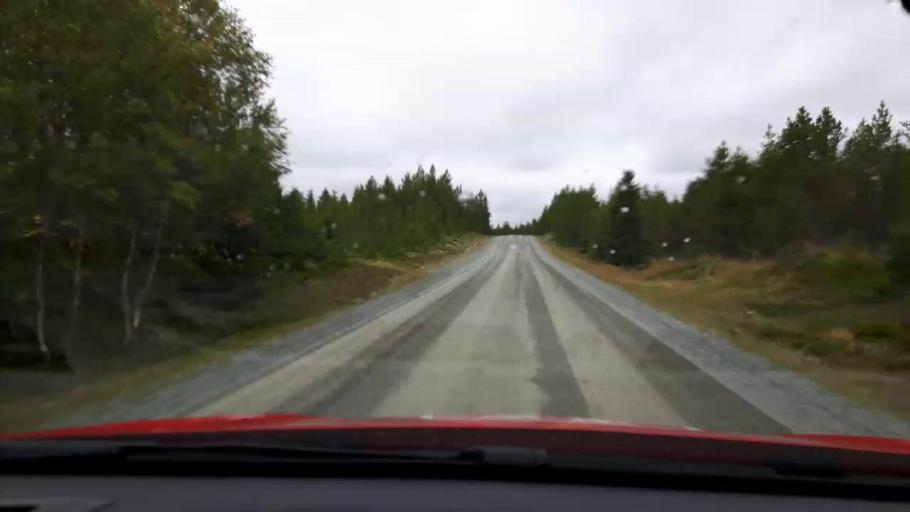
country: SE
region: Jaemtland
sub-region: Bergs Kommun
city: Hoverberg
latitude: 62.9046
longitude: 14.0690
